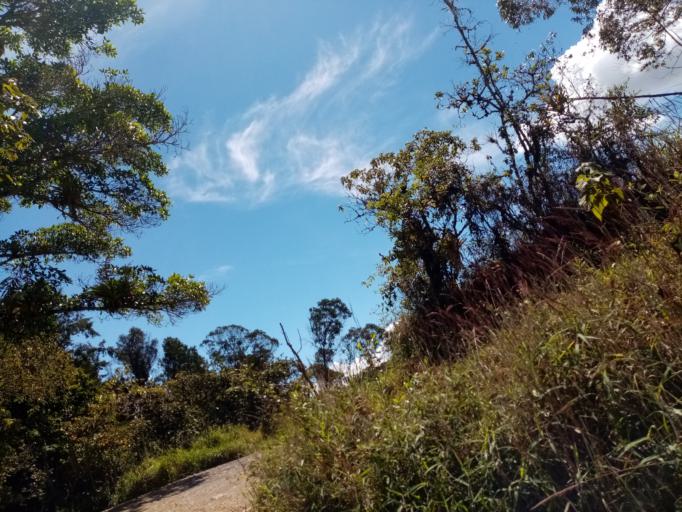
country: CO
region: Cundinamarca
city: Tenza
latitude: 5.0685
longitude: -73.4270
